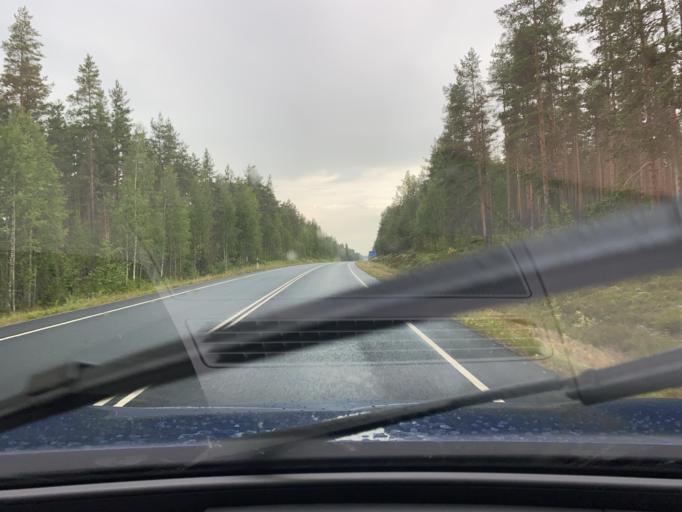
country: FI
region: Central Ostrobothnia
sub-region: Kaustinen
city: Veteli
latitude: 63.4123
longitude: 23.9547
